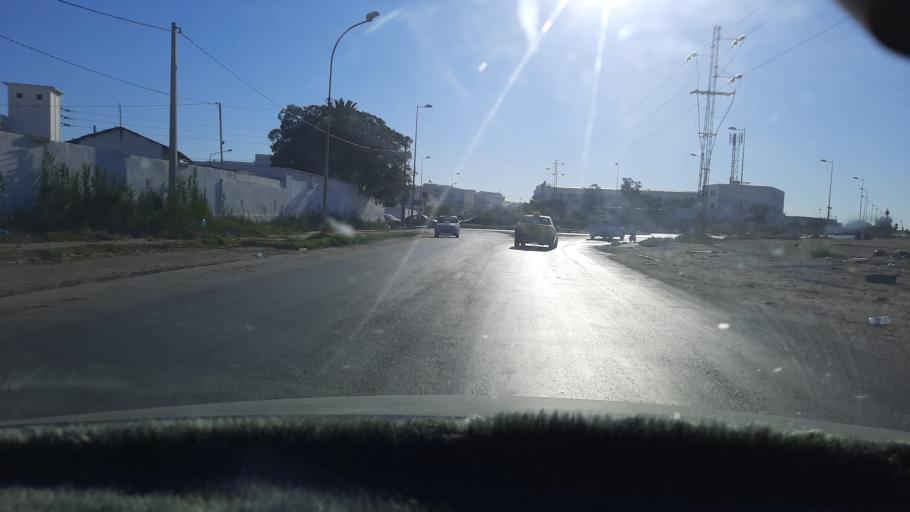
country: TN
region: Safaqis
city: Sfax
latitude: 34.7274
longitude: 10.7496
